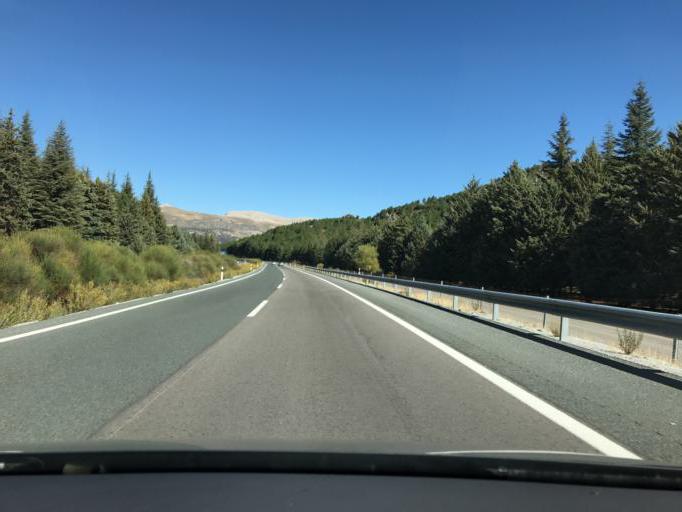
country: ES
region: Andalusia
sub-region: Provincia de Granada
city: Beas de Granada
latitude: 37.2755
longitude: -3.4590
